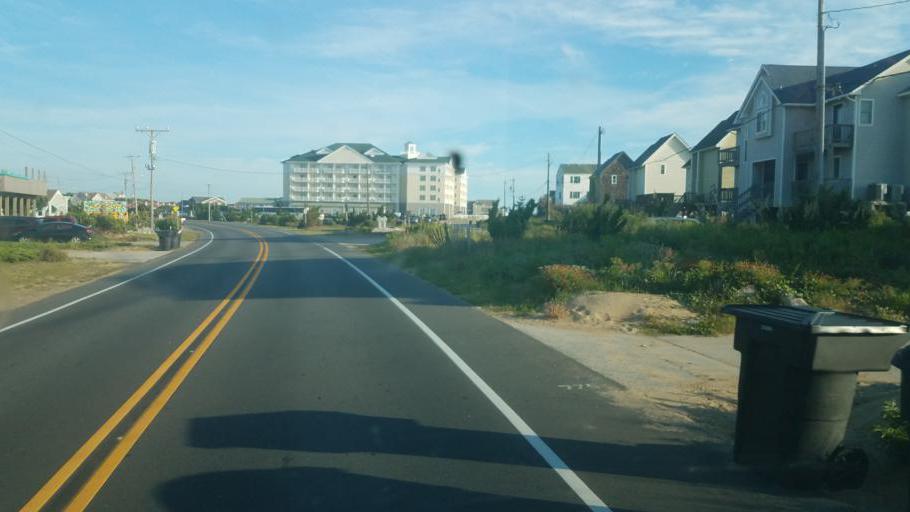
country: US
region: North Carolina
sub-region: Dare County
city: Kitty Hawk
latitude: 36.0987
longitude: -75.7103
